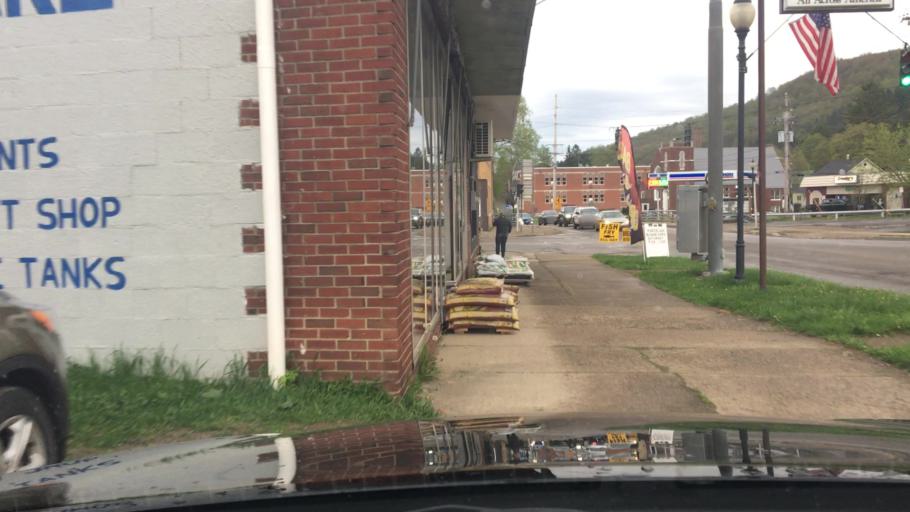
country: US
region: New York
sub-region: Cattaraugus County
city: Little Valley
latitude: 42.2497
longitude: -78.7991
